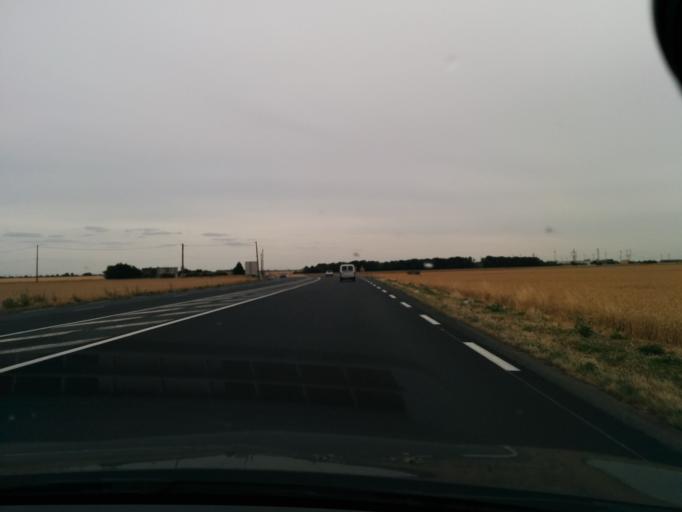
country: FR
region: Ile-de-France
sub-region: Departement de l'Essonne
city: Angerville
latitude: 48.2905
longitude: 1.9826
